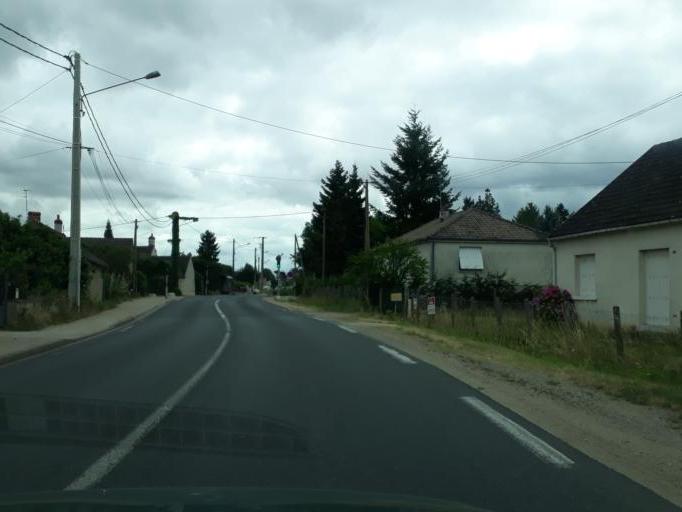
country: FR
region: Centre
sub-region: Departement du Loiret
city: Sandillon
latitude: 47.8508
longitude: 2.0213
